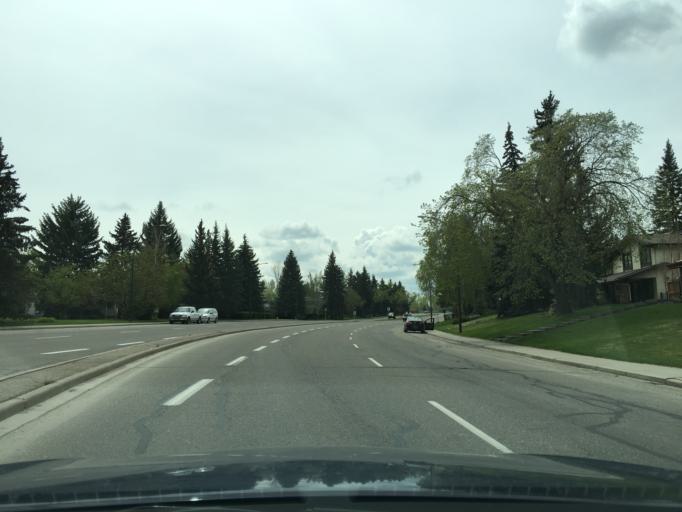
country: CA
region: Alberta
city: Calgary
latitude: 50.9471
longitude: -114.0846
